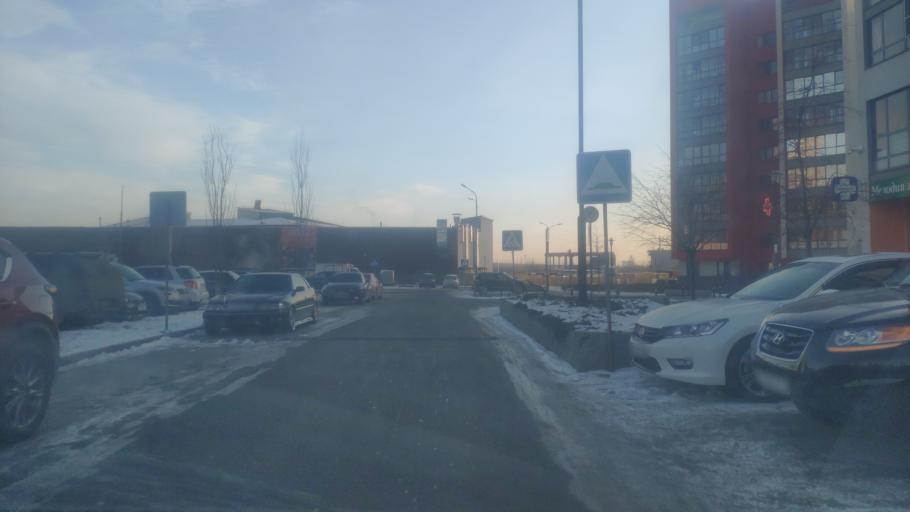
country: RU
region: Tjumen
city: Tyumen
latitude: 57.1723
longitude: 65.5647
